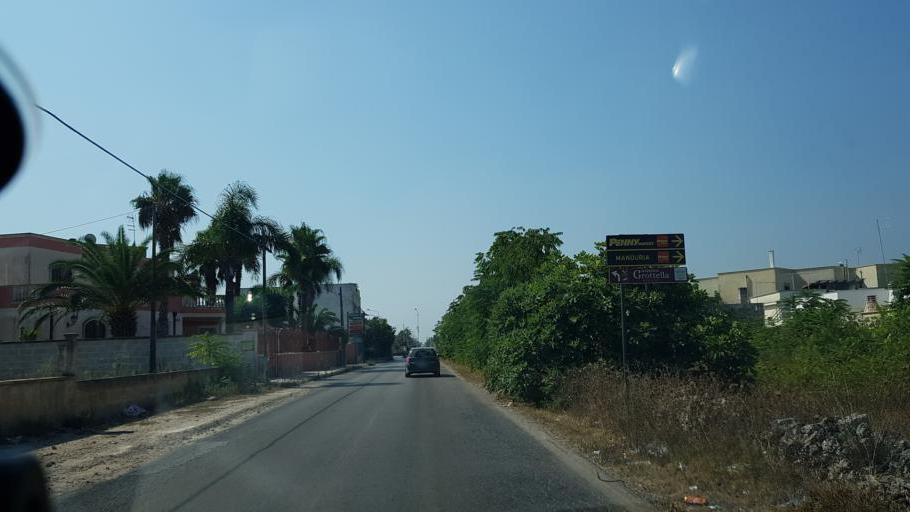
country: IT
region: Apulia
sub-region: Provincia di Taranto
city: Manduria
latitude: 40.4113
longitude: 17.6312
